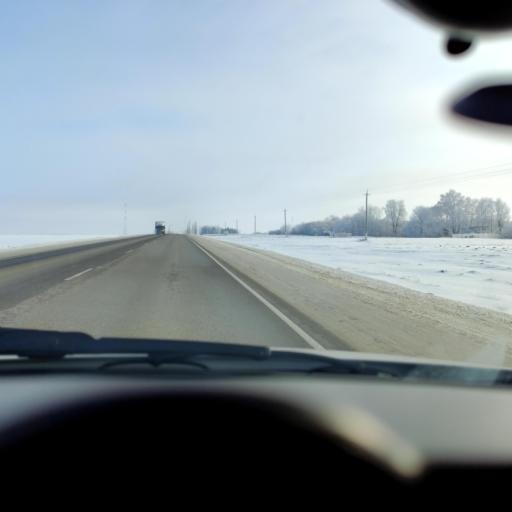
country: RU
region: Belgorod
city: Troitskiy
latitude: 51.6171
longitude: 37.5194
